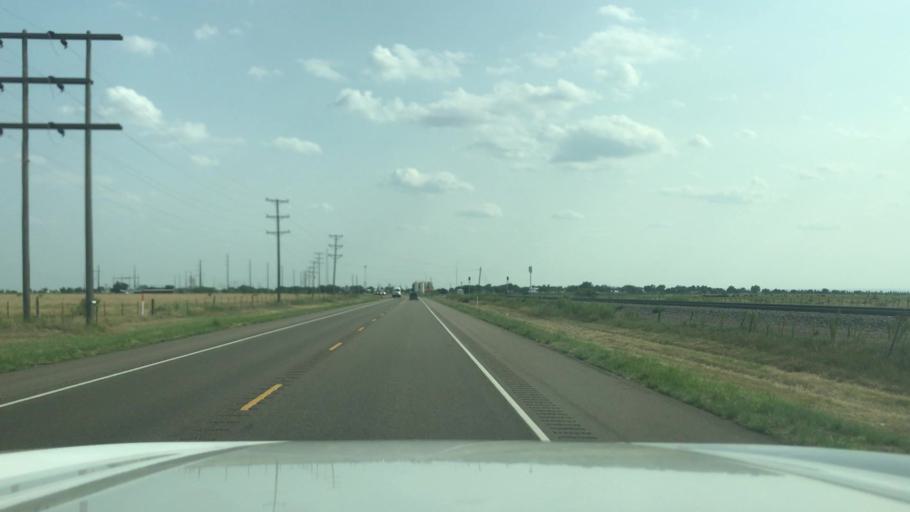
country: US
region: Texas
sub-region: Hartley County
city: Channing
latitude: 35.6979
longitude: -102.3273
